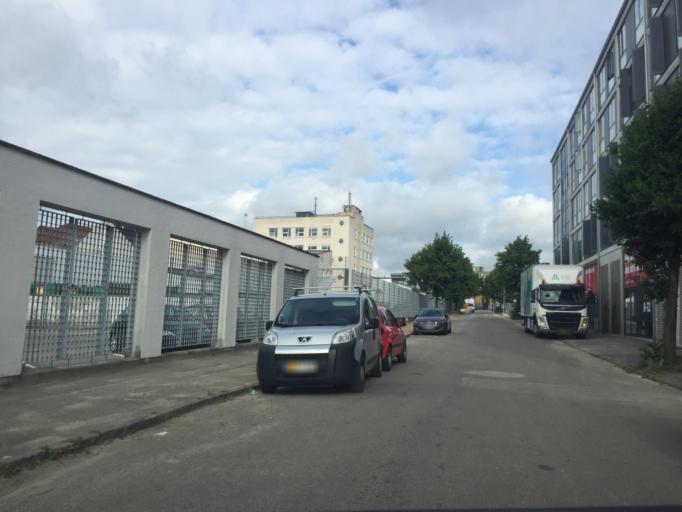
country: DK
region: Capital Region
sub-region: Frederiksberg Kommune
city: Frederiksberg
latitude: 55.7074
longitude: 12.5319
